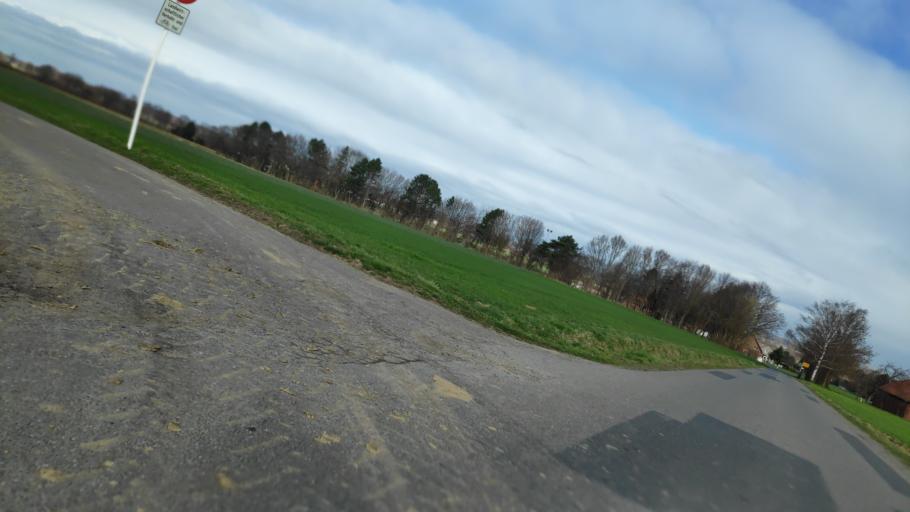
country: DE
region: North Rhine-Westphalia
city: Bad Oeynhausen
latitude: 52.2674
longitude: 8.8205
